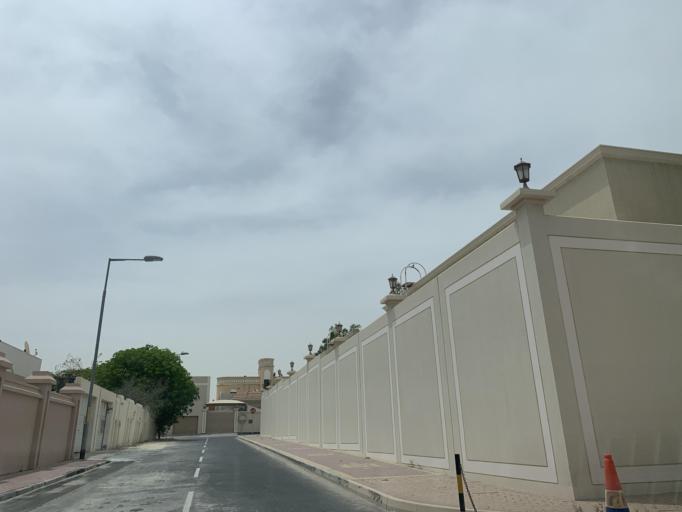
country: BH
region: Northern
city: Ar Rifa'
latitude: 26.1395
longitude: 50.5503
